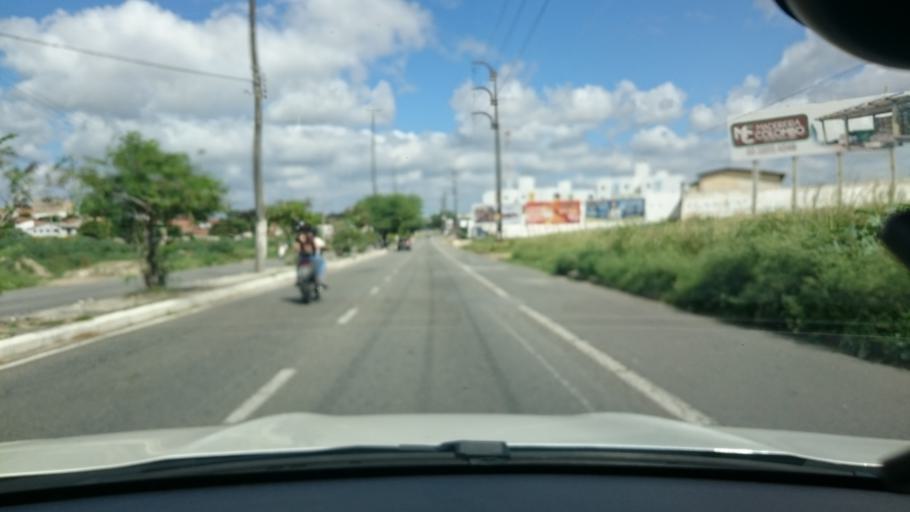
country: BR
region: Paraiba
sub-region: Campina Grande
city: Campina Grande
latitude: -7.2301
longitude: -35.9072
